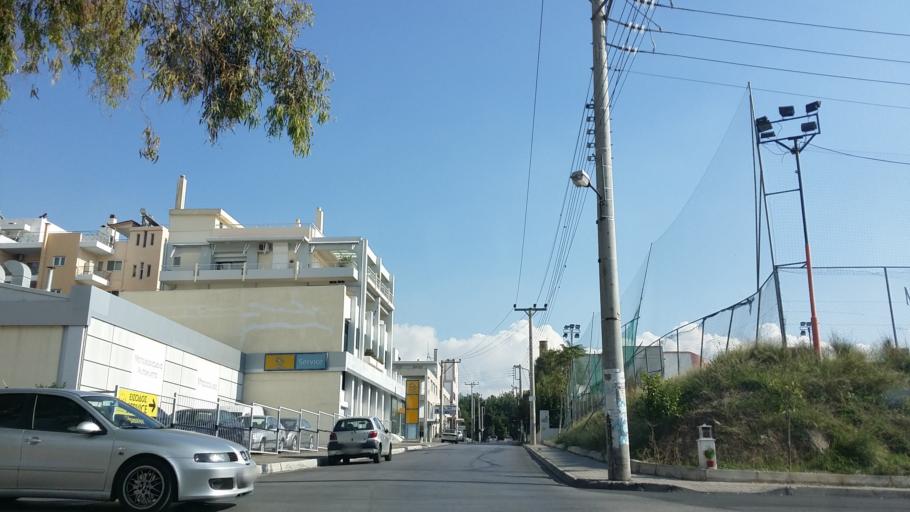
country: GR
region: Attica
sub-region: Nomarchia Athinas
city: Nea Filadelfeia
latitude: 38.0486
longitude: 23.7444
